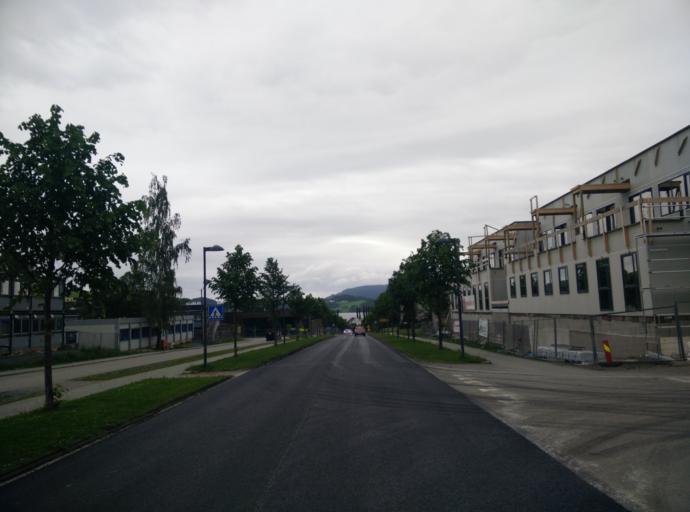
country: NO
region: Sor-Trondelag
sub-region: Skaun
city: Borsa
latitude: 63.3239
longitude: 10.0647
